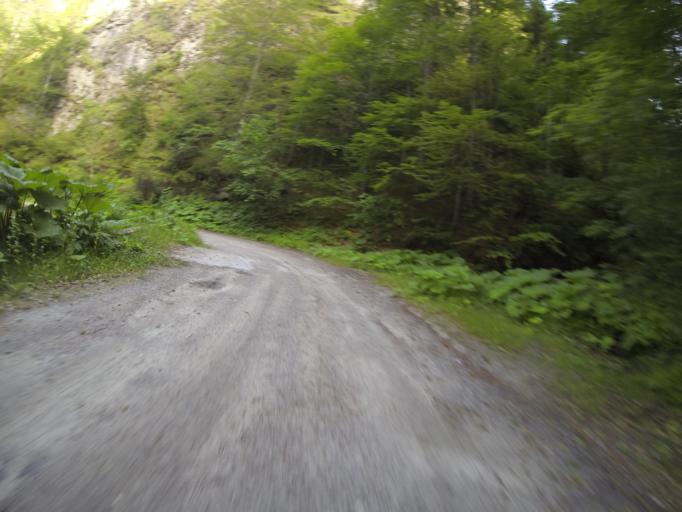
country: RO
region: Valcea
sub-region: Oras Baile Olanesti
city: Baile Olanesti
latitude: 45.2533
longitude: 24.1721
